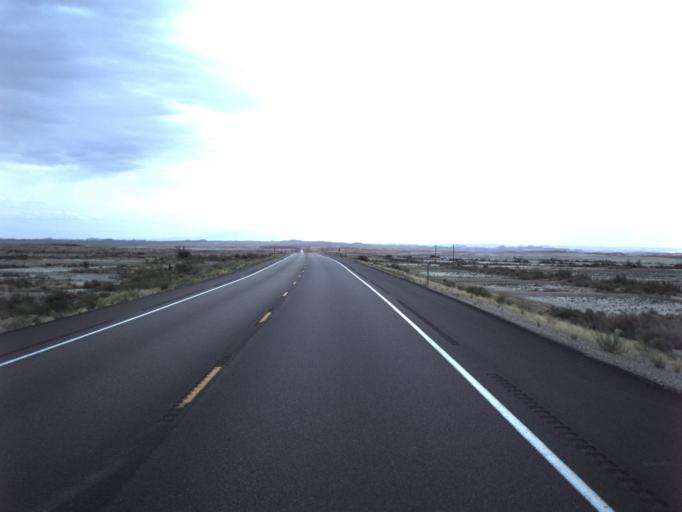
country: US
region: Utah
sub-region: Carbon County
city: East Carbon City
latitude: 39.0022
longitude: -110.2712
